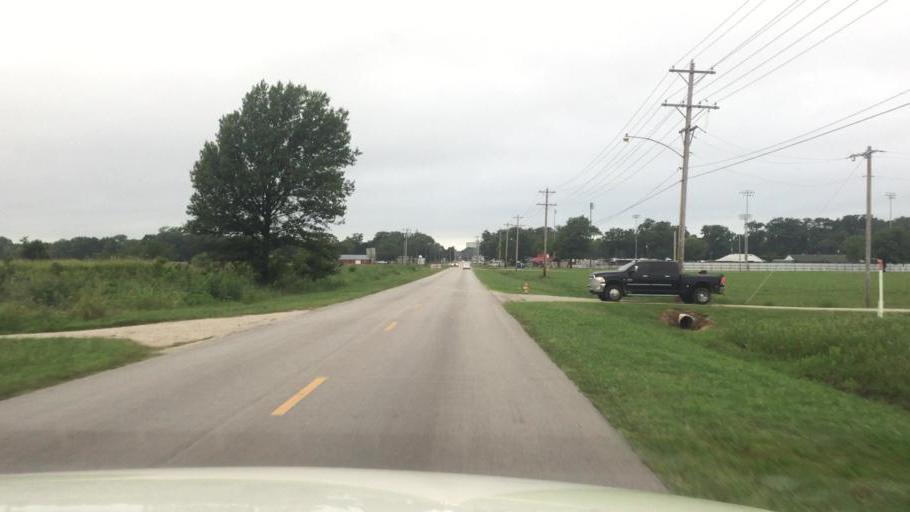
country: US
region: Kansas
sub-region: Montgomery County
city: Coffeyville
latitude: 37.0354
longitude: -95.5888
